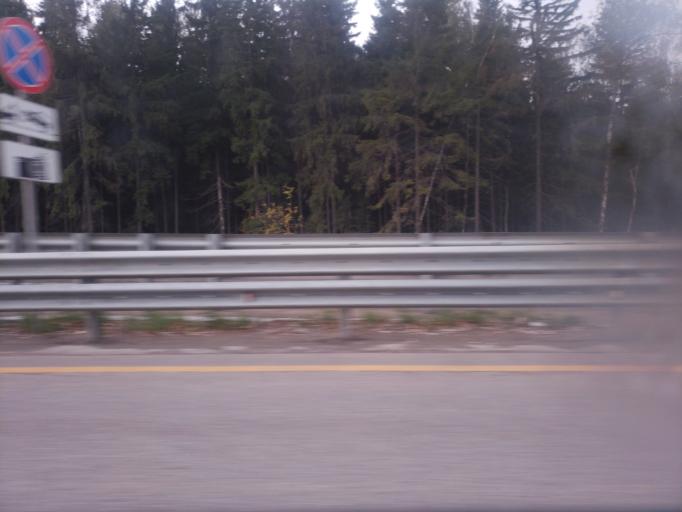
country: RU
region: Moskovskaya
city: Vostryakovo
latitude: 55.4378
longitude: 37.8717
